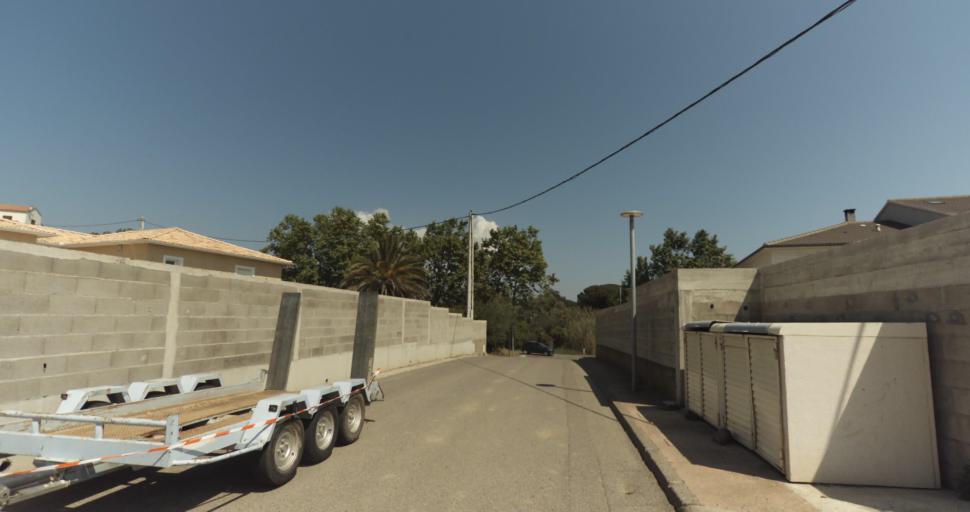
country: FR
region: Corsica
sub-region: Departement de la Haute-Corse
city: Biguglia
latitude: 42.6186
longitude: 9.4342
